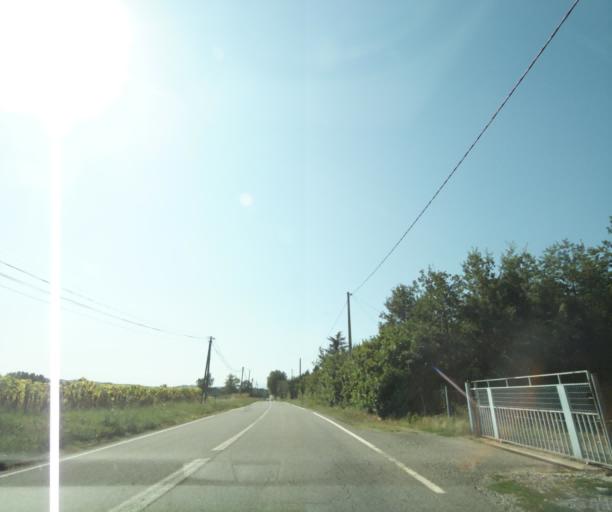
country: FR
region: Midi-Pyrenees
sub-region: Departement de la Haute-Garonne
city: Saint-Sulpice-sur-Leze
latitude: 43.3141
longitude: 1.3235
